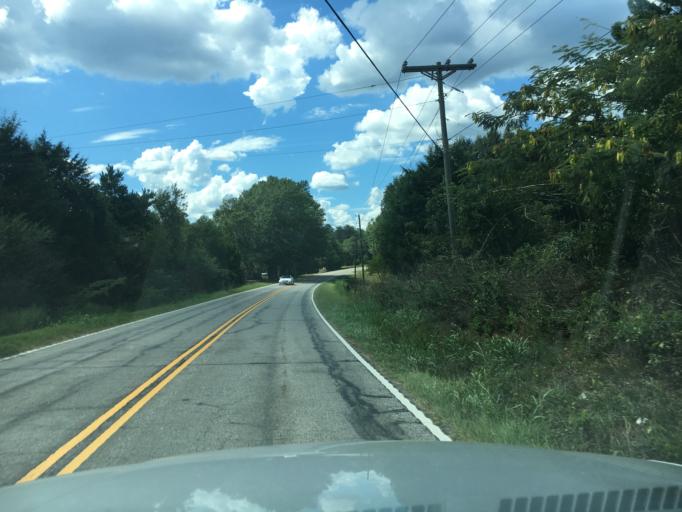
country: US
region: South Carolina
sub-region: Laurens County
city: Laurens
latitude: 34.5184
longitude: -82.1072
